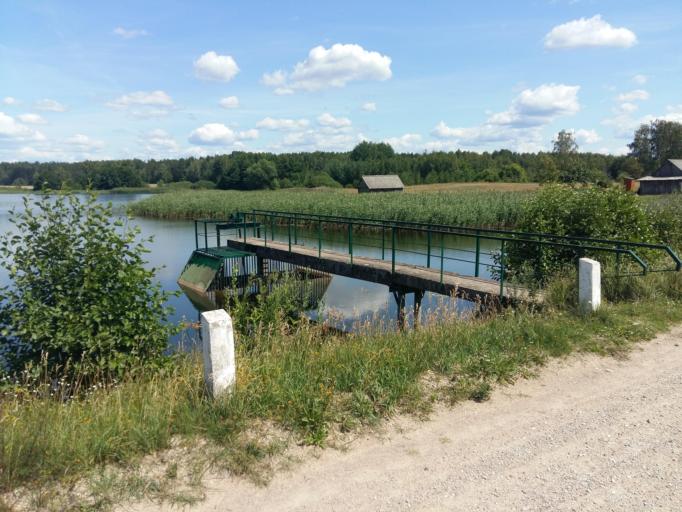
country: LT
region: Alytaus apskritis
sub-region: Alytaus rajonas
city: Daugai
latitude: 54.2120
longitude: 24.2248
